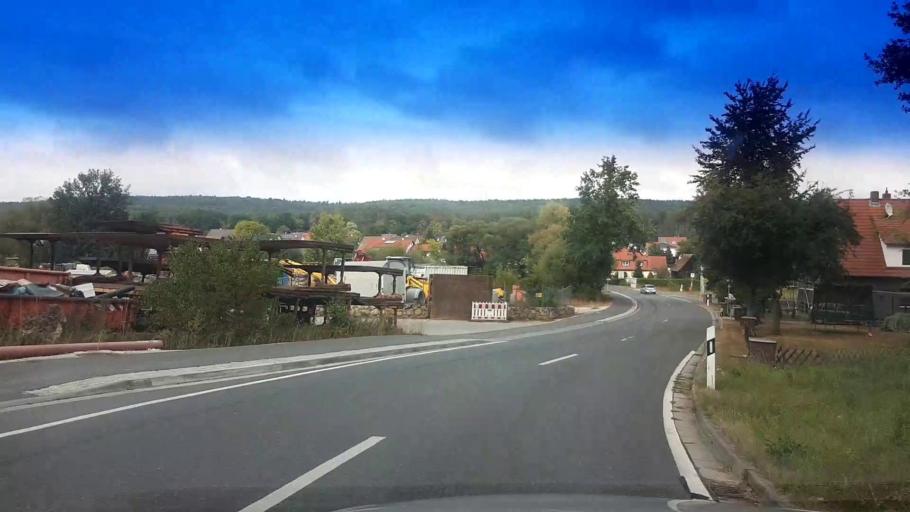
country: DE
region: Bavaria
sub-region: Upper Franconia
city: Heroldsbach
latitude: 49.7028
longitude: 11.0107
